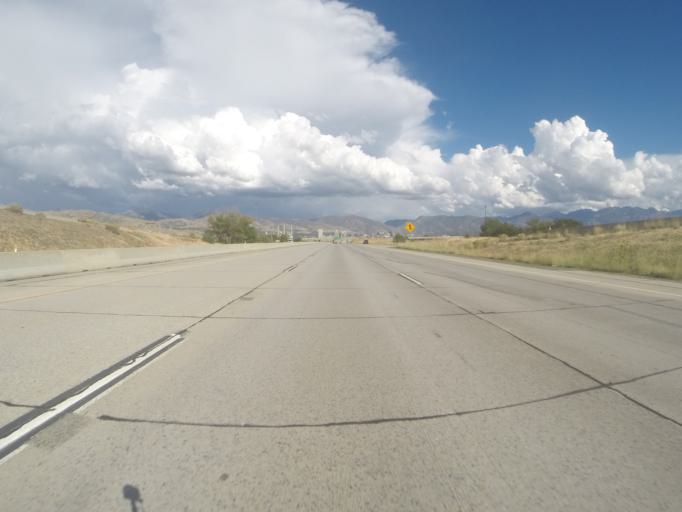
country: US
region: Utah
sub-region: Salt Lake County
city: Salt Lake City
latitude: 40.7657
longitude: -111.9470
